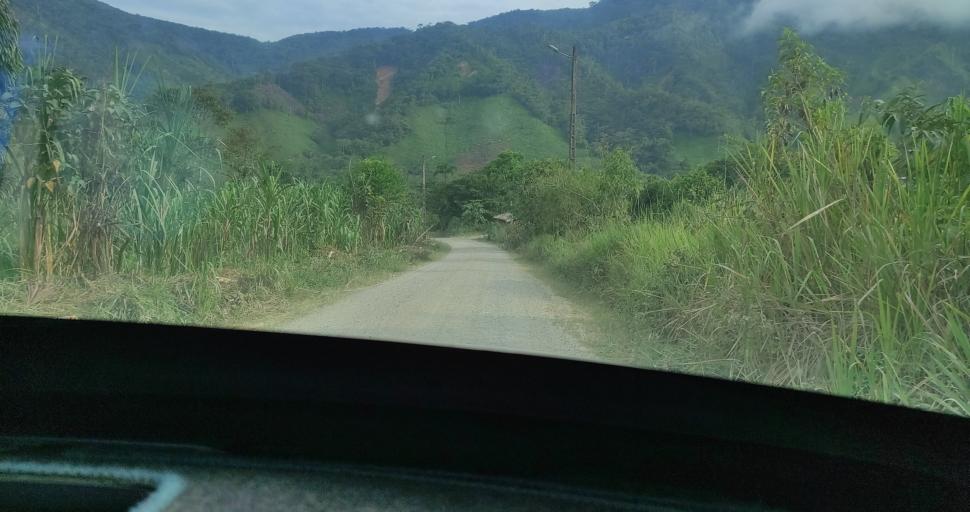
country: EC
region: Zamora-Chinchipe
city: Yantzaza
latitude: -3.7735
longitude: -78.8944
